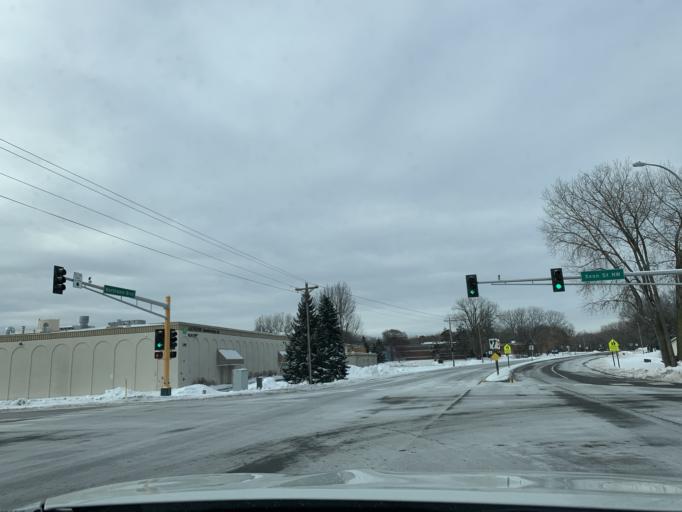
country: US
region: Minnesota
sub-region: Anoka County
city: Andover
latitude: 45.1814
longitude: -93.2978
